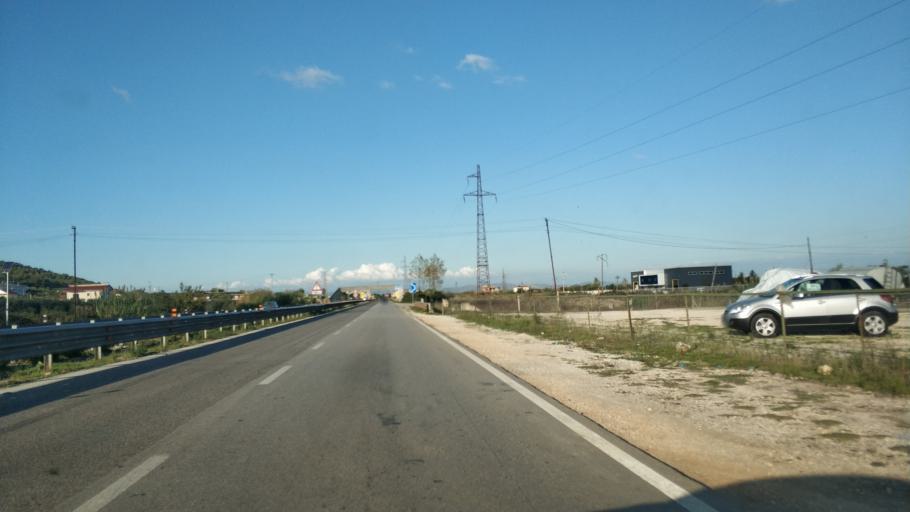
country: AL
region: Fier
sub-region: Rrethi i Lushnjes
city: Kolonje
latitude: 40.7951
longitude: 19.6040
